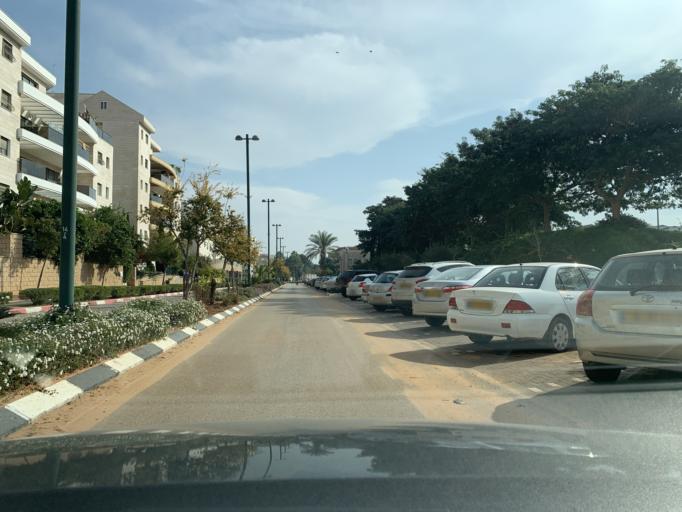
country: IL
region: Central District
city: Kfar Saba
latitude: 32.1854
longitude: 34.9260
